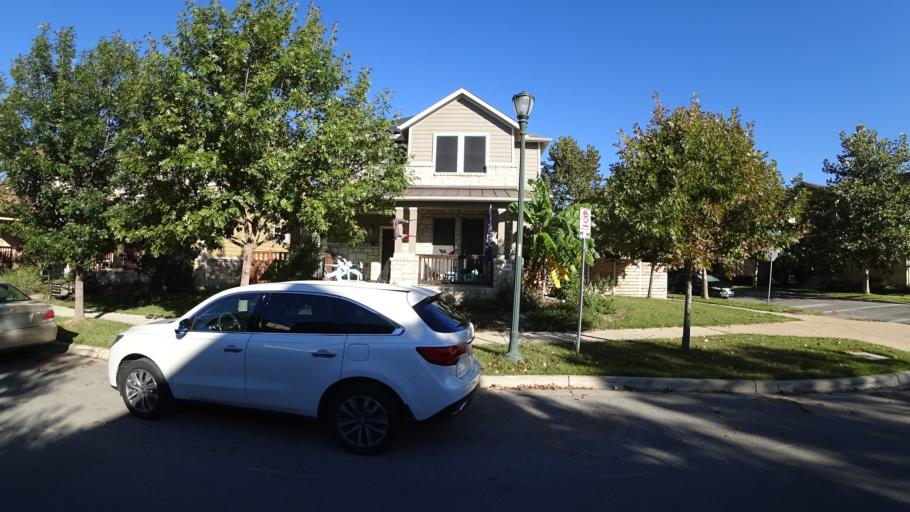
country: US
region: Texas
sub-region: Travis County
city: Austin
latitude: 30.2916
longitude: -97.7004
